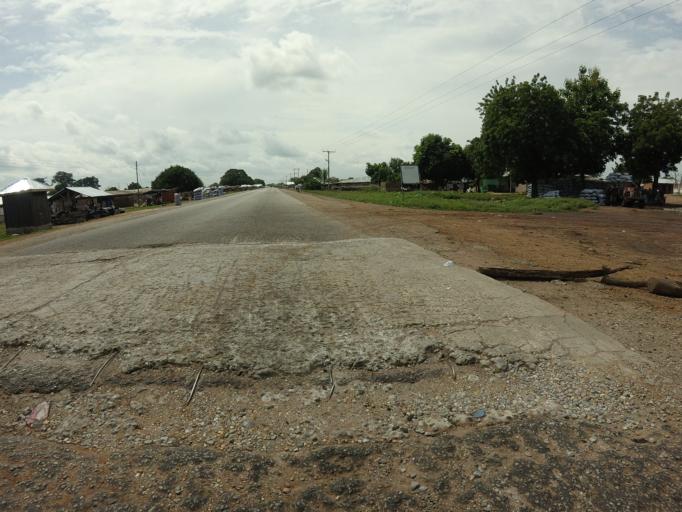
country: GH
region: Brong-Ahafo
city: Kintampo
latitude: 8.4462
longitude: -1.5646
